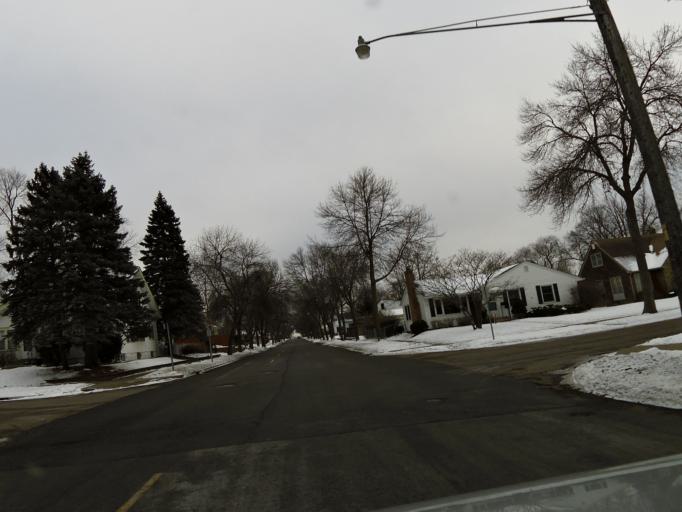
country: US
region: Minnesota
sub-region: Dakota County
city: Mendota Heights
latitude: 44.9236
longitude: -93.1925
